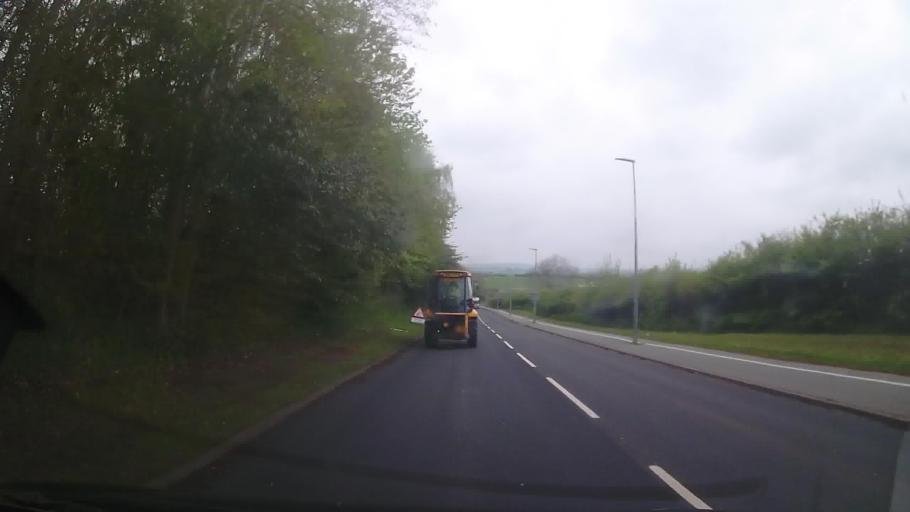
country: GB
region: Wales
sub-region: Wrexham
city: Ruabon
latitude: 52.9849
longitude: -3.0534
